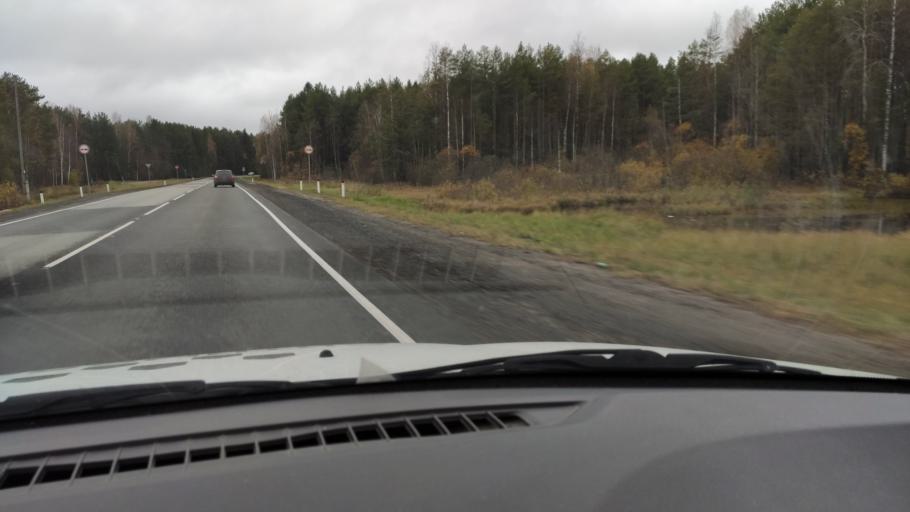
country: RU
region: Kirov
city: Belaya Kholunitsa
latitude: 58.8742
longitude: 50.8603
